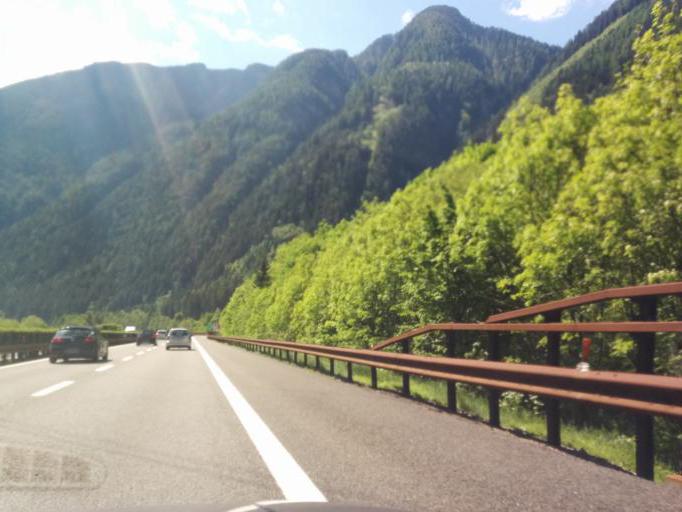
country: IT
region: Trentino-Alto Adige
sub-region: Bolzano
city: Campo di Trens
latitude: 46.8212
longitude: 11.5374
